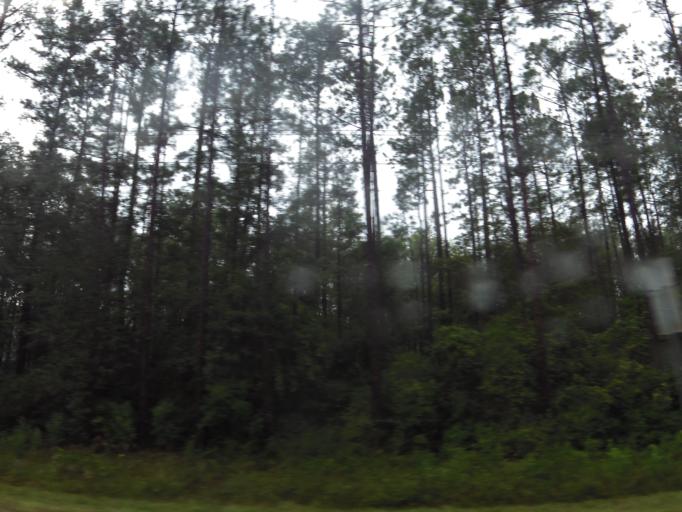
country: US
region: Florida
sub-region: Baker County
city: Macclenny
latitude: 30.3688
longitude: -82.1382
